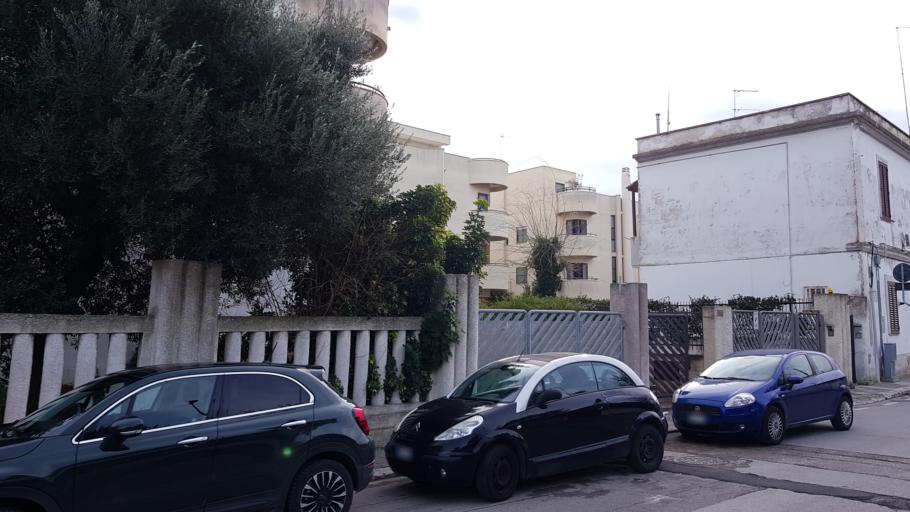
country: IT
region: Apulia
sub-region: Provincia di Brindisi
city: Materdomini
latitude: 40.6494
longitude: 17.9461
